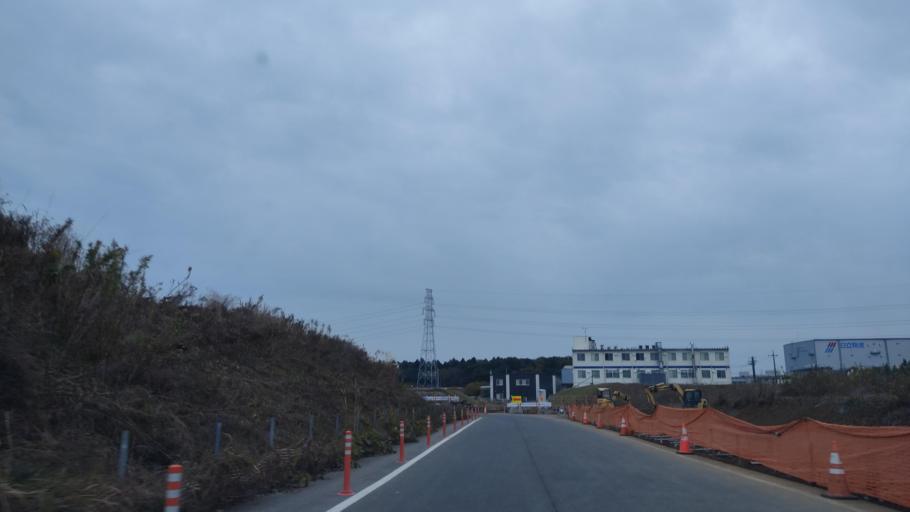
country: JP
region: Ibaraki
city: Moriya
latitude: 35.9070
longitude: 139.9538
